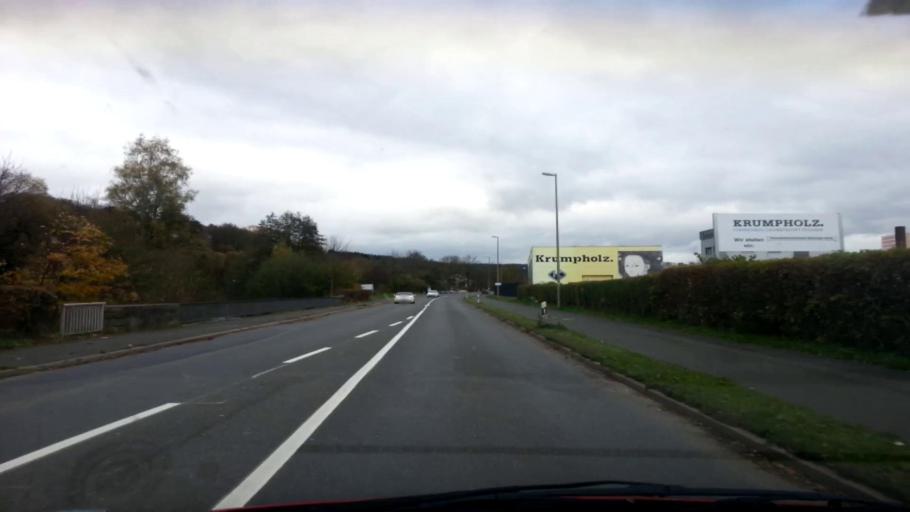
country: DE
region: Bavaria
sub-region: Upper Franconia
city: Kronach
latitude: 50.2408
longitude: 11.3339
